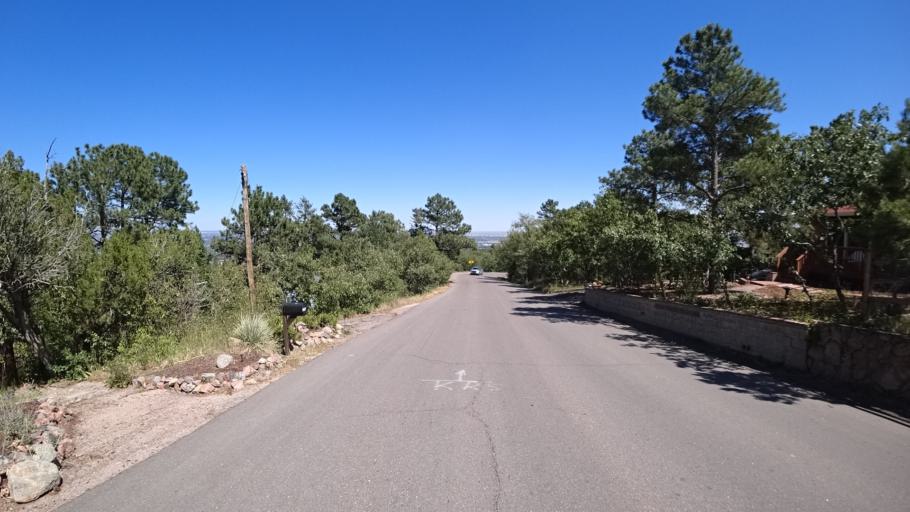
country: US
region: Colorado
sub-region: El Paso County
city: Colorado Springs
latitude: 38.7792
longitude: -104.8602
